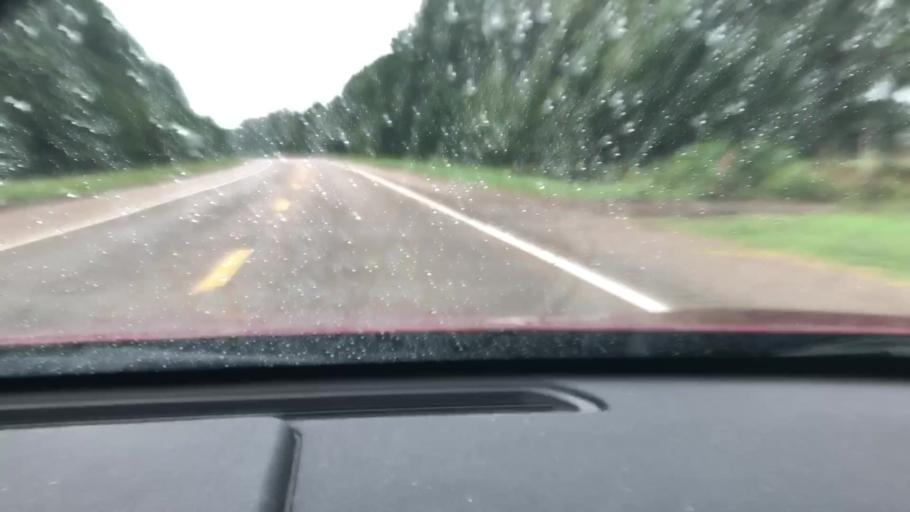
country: US
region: Arkansas
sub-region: Columbia County
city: Magnolia
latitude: 33.2984
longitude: -93.2628
